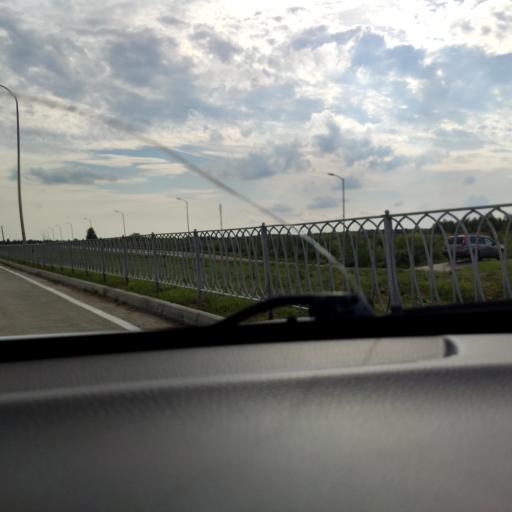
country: RU
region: Tatarstan
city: Sviyazhsk
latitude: 55.7474
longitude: 48.7395
